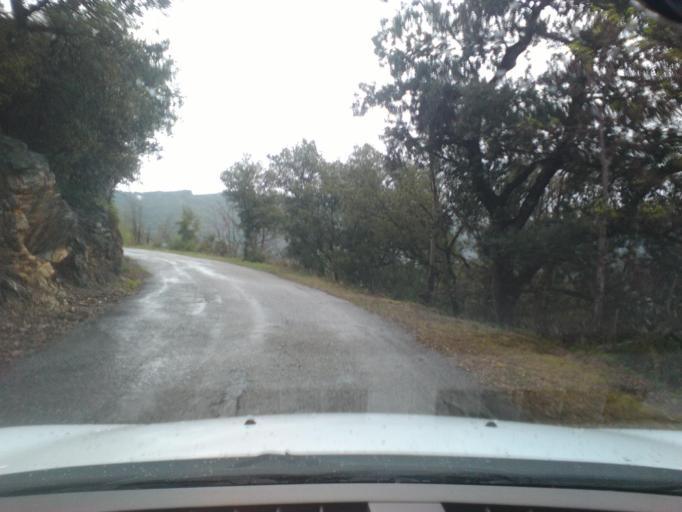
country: FR
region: Languedoc-Roussillon
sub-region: Departement du Gard
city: Sumene
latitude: 44.0253
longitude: 3.6939
